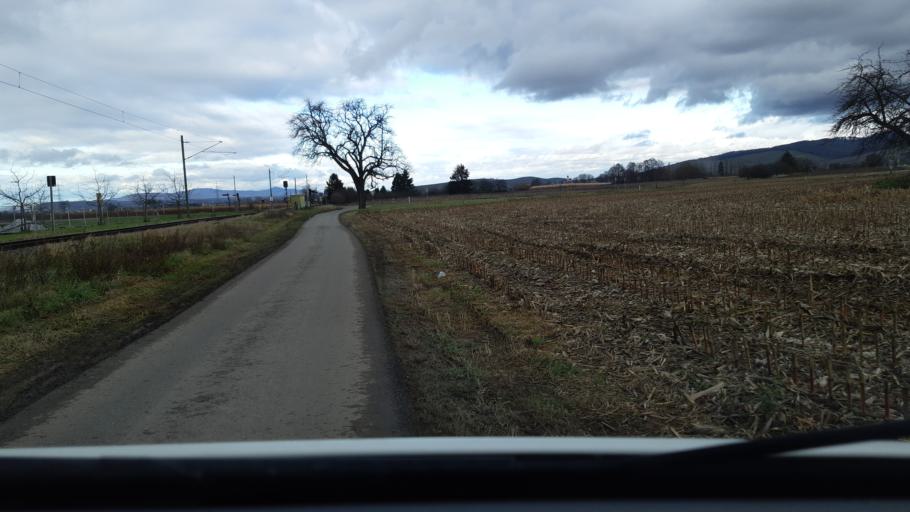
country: DE
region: Baden-Wuerttemberg
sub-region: Freiburg Region
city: Bad Krozingen
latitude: 47.8905
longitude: 7.7275
